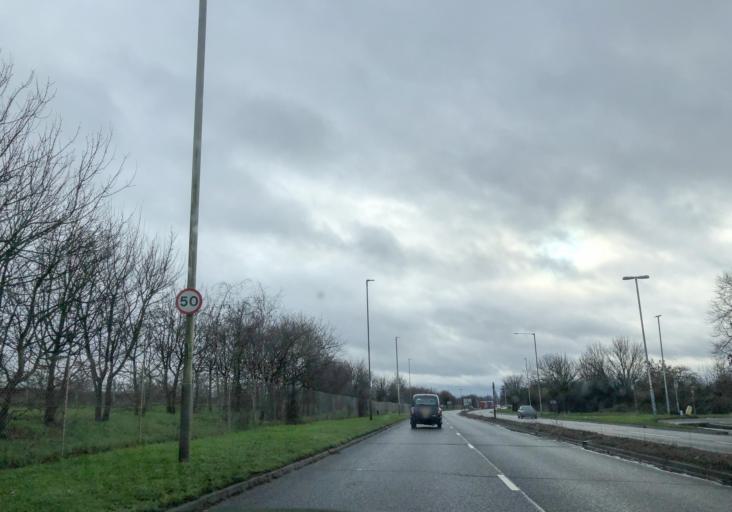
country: GB
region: England
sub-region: Buckinghamshire
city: Iver
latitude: 51.4686
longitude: -0.4918
